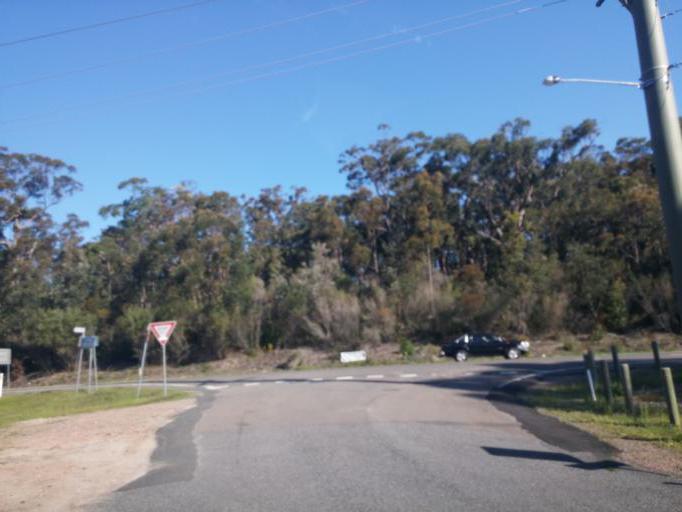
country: AU
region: New South Wales
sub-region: Port Stephens Shire
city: Corlette
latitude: -32.7382
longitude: 152.1214
